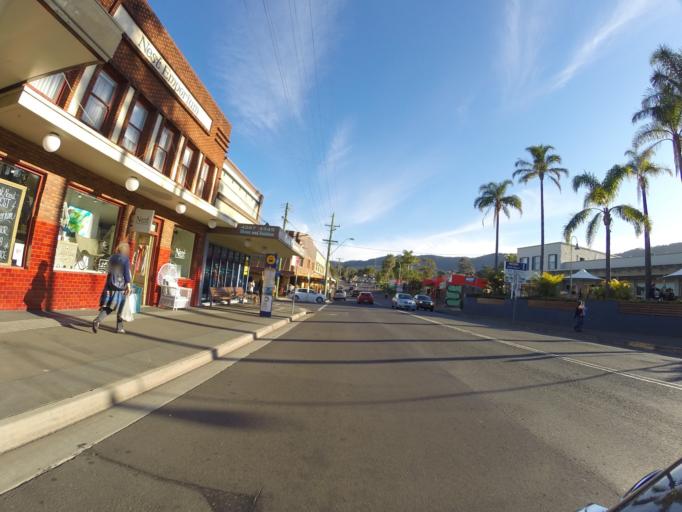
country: AU
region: New South Wales
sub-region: Wollongong
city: Bulli
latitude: -34.3152
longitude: 150.9229
